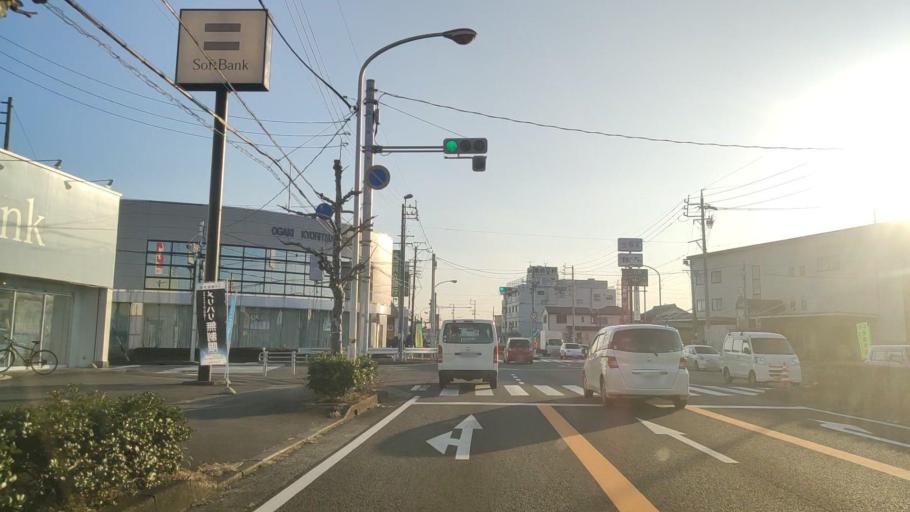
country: JP
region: Gifu
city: Gifu-shi
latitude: 35.4288
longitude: 136.7320
